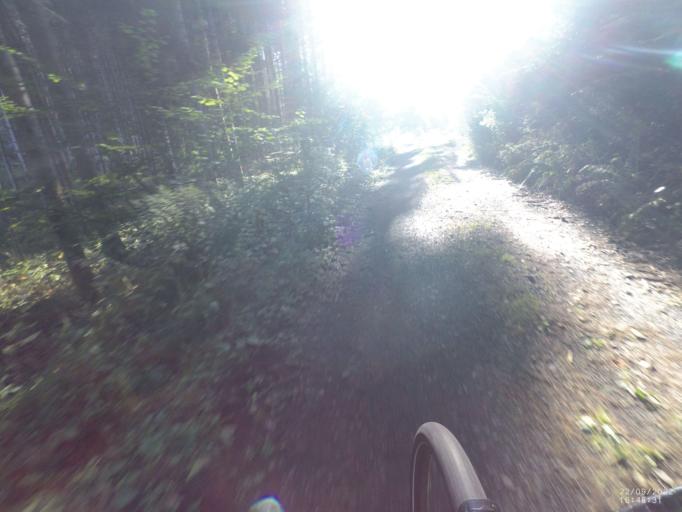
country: DE
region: Rheinland-Pfalz
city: Udersdorf
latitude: 50.1661
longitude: 6.8021
